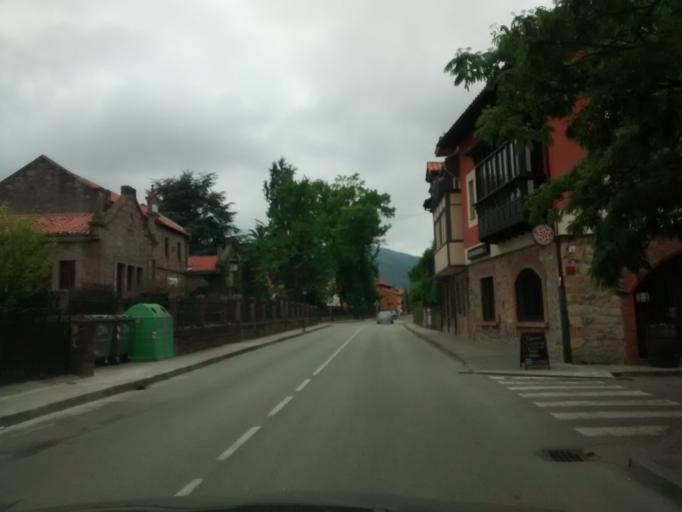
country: ES
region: Cantabria
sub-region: Provincia de Cantabria
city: Cabezon de la Sal
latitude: 43.3044
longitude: -4.2378
